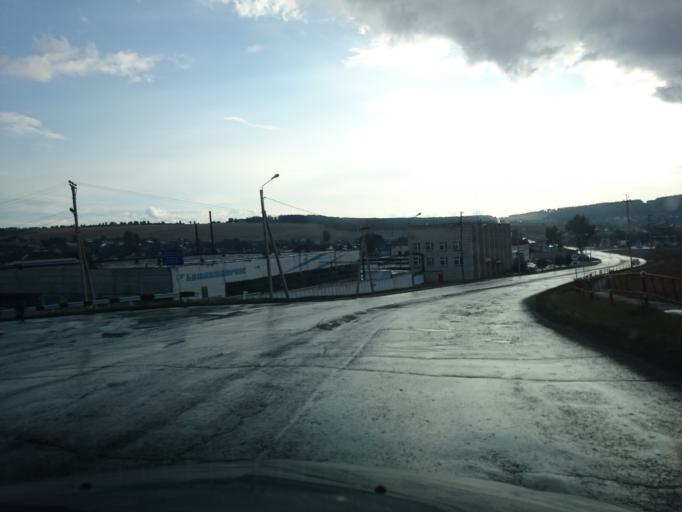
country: RU
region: Bashkortostan
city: Lomovka
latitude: 53.9560
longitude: 58.3590
